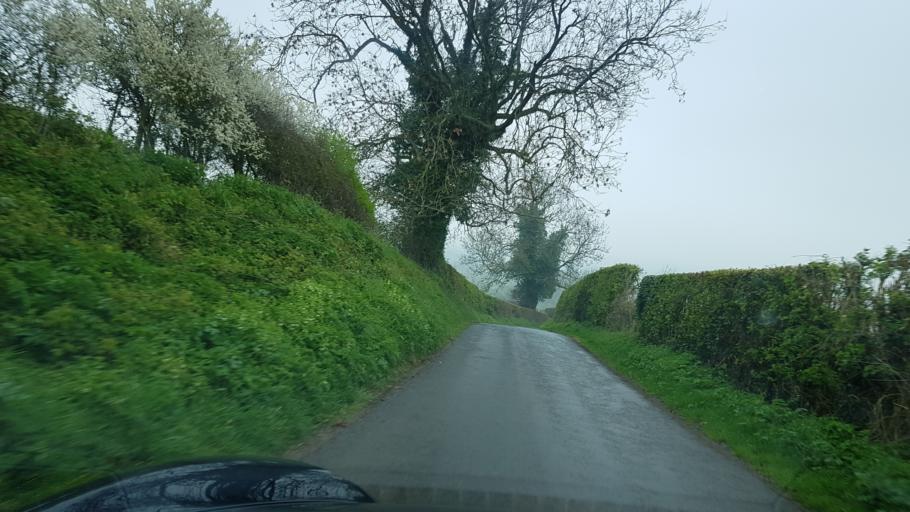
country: GB
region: England
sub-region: Herefordshire
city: Yatton
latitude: 52.0250
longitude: -2.5343
